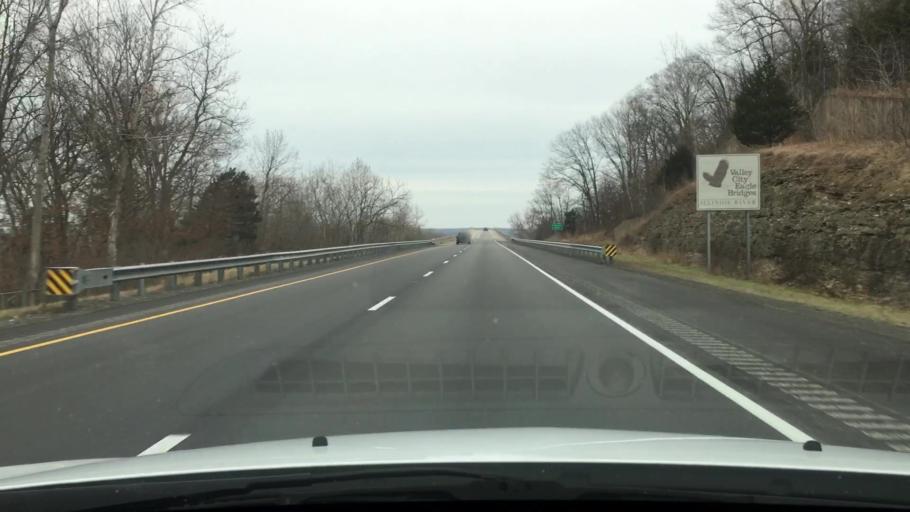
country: US
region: Illinois
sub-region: Pike County
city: Griggsville
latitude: 39.6845
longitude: -90.6467
